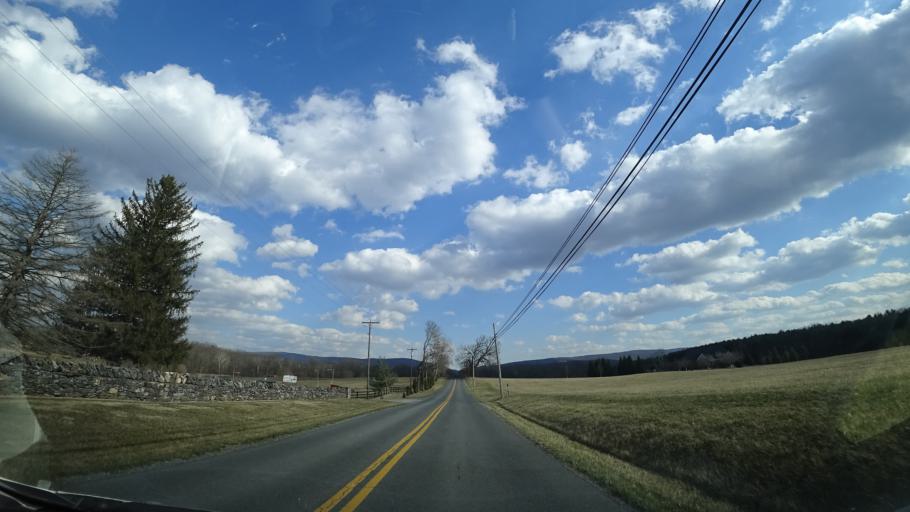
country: US
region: Virginia
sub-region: Warren County
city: Shenandoah Farms
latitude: 39.0551
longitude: -78.0182
